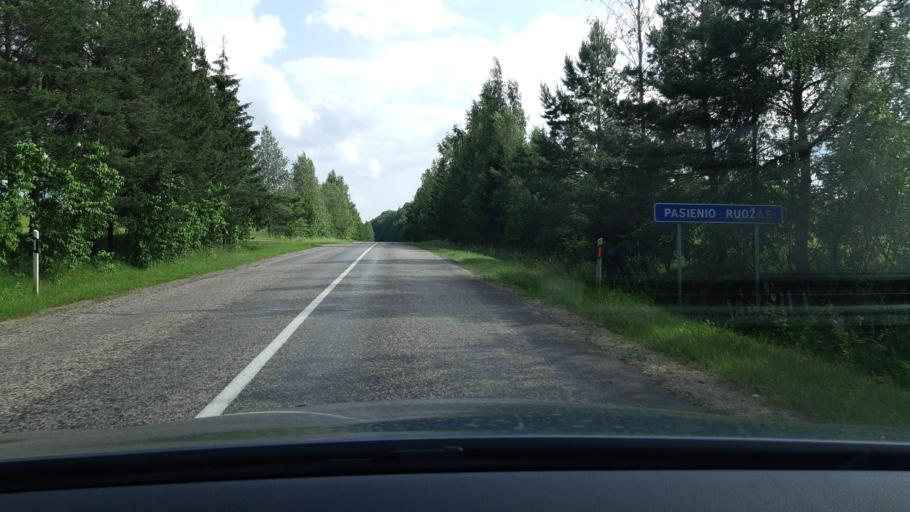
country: LT
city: Kybartai
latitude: 54.4977
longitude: 22.7118
